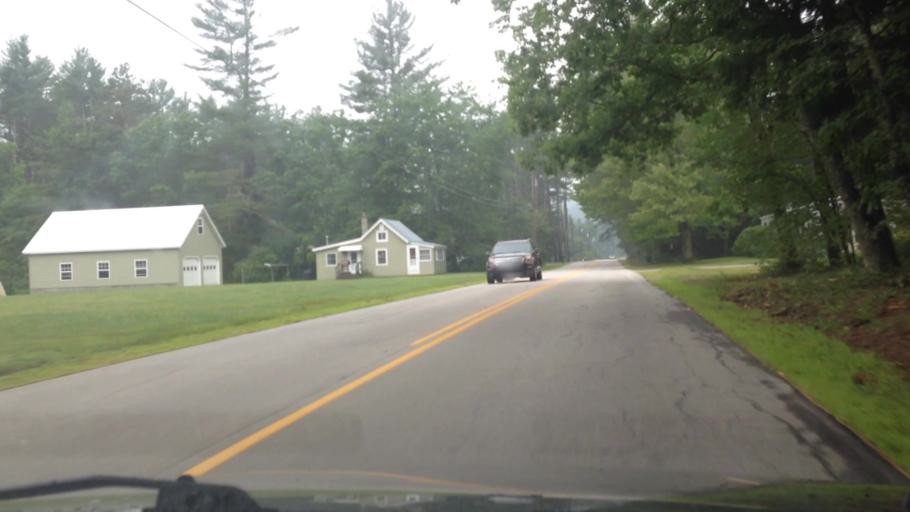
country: US
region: New Hampshire
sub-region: Cheshire County
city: Swanzey
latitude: 42.8453
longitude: -72.2699
